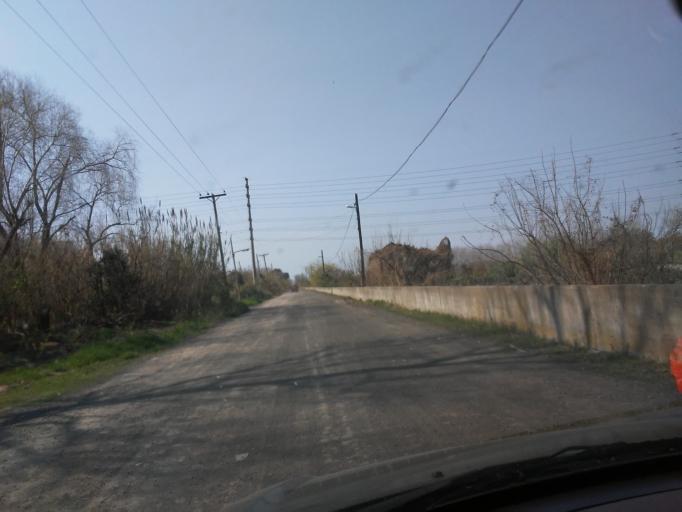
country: AR
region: Buenos Aires
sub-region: Partido de Avellaneda
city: Avellaneda
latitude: -34.6759
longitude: -58.3101
